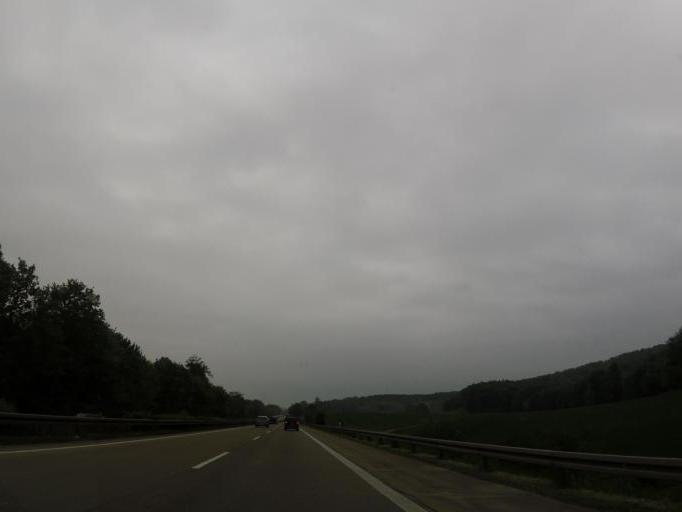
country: DE
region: Lower Saxony
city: Seesen
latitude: 51.8716
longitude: 10.1267
